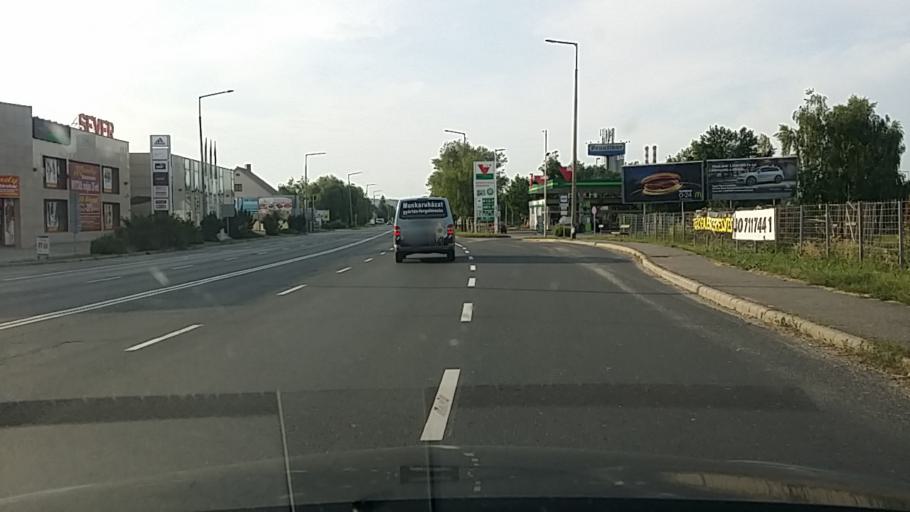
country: HU
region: Borsod-Abauj-Zemplen
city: Miskolc
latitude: 48.0554
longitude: 20.7980
